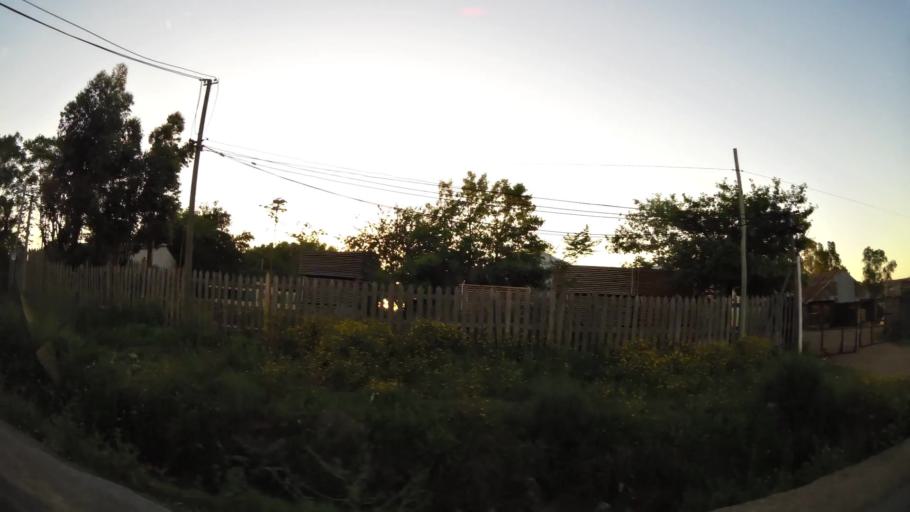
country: UY
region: Montevideo
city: Montevideo
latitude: -34.8268
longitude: -56.1684
